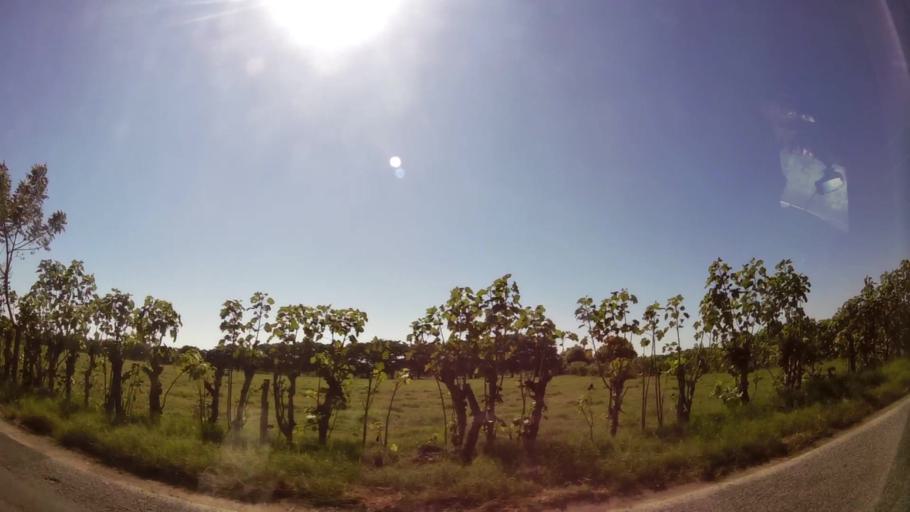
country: GT
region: Escuintla
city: Iztapa
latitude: 13.9245
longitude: -90.5884
